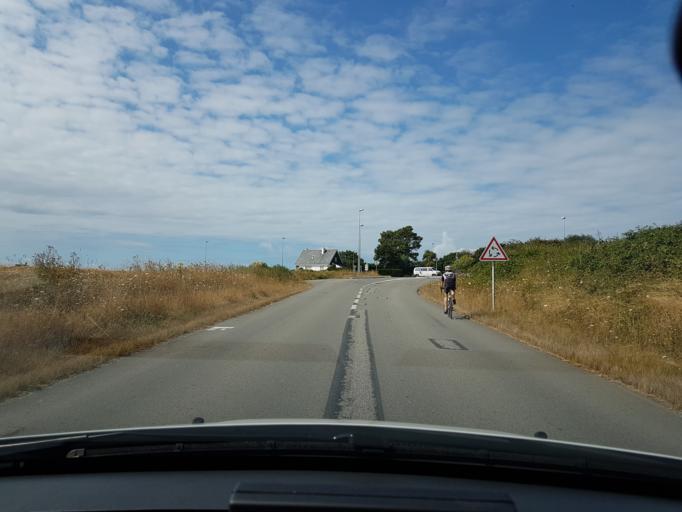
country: FR
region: Brittany
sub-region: Departement du Morbihan
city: Sainte-Helene
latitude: 47.7066
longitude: -3.2184
